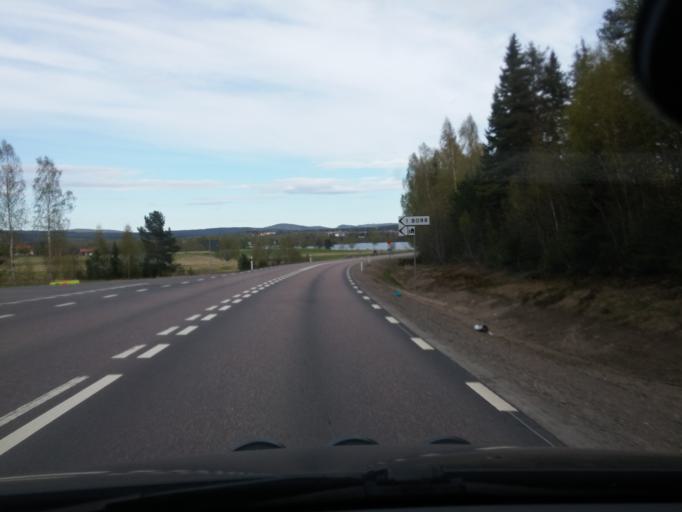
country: SE
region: Gaevleborg
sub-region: Ljusdals Kommun
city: Ljusdal
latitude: 61.8251
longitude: 16.0357
